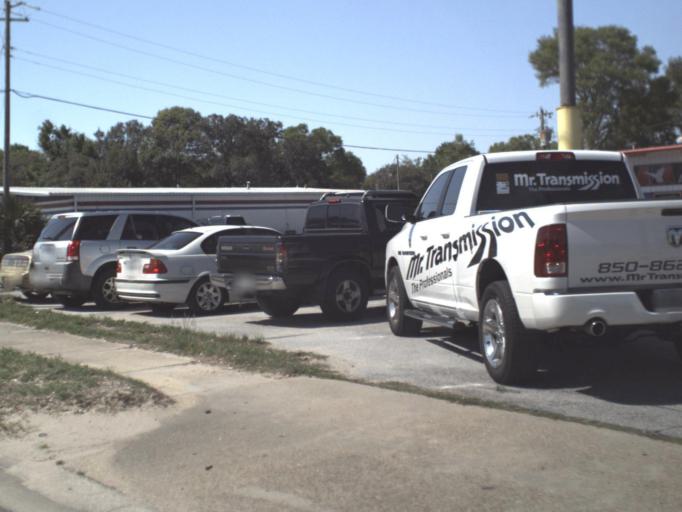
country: US
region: Florida
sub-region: Okaloosa County
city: Ocean City
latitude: 30.4464
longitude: -86.6077
